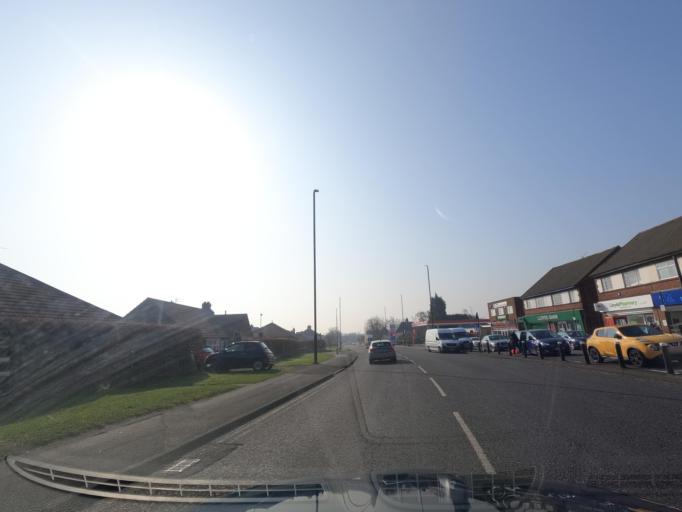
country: GB
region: England
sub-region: Newcastle upon Tyne
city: Gosforth
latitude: 55.0079
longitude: -1.5782
